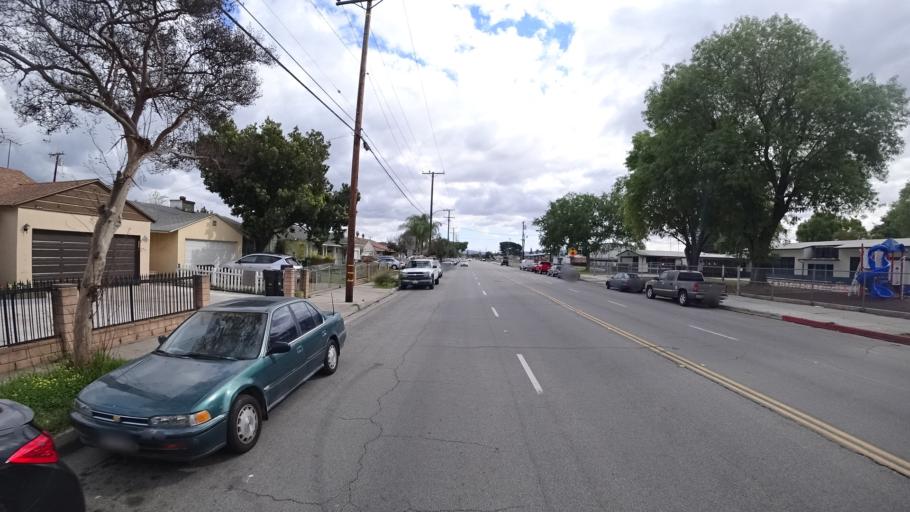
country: US
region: California
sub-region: Los Angeles County
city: Baldwin Park
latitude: 34.0904
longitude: -117.9735
